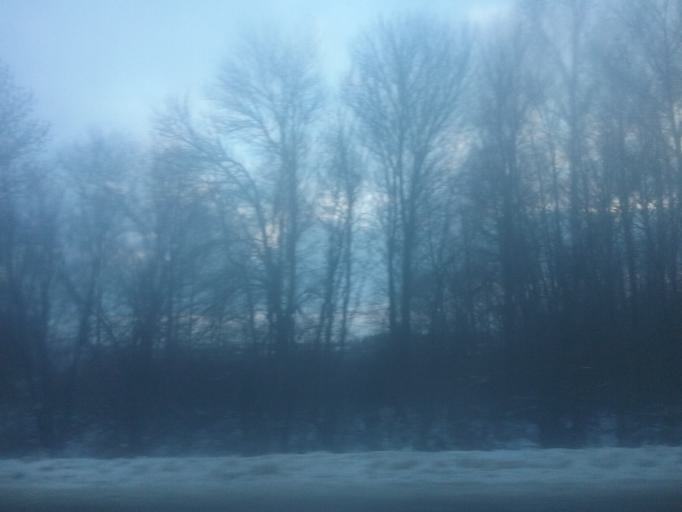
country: RU
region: Tula
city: Brusyanka
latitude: 54.0243
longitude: 37.9919
